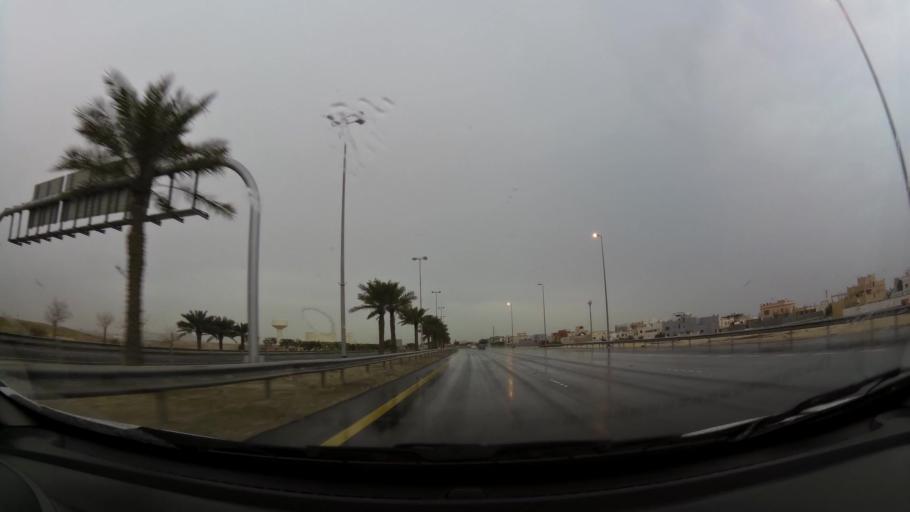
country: BH
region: Central Governorate
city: Dar Kulayb
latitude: 26.0788
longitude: 50.5148
